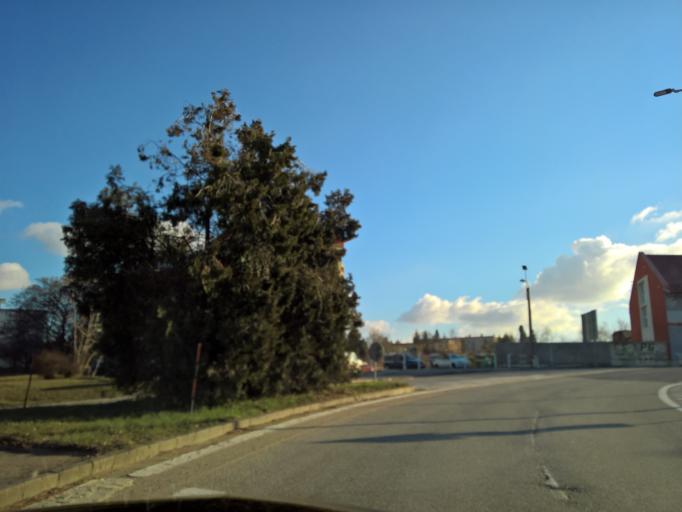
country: SK
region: Nitriansky
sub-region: Okres Nitra
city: Nitra
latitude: 48.3088
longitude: 18.0740
